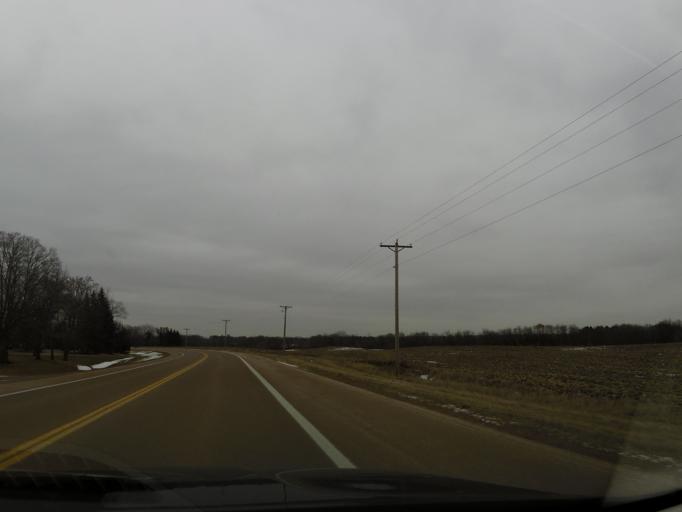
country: US
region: Minnesota
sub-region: Carver County
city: Watertown
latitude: 44.9679
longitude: -93.7866
